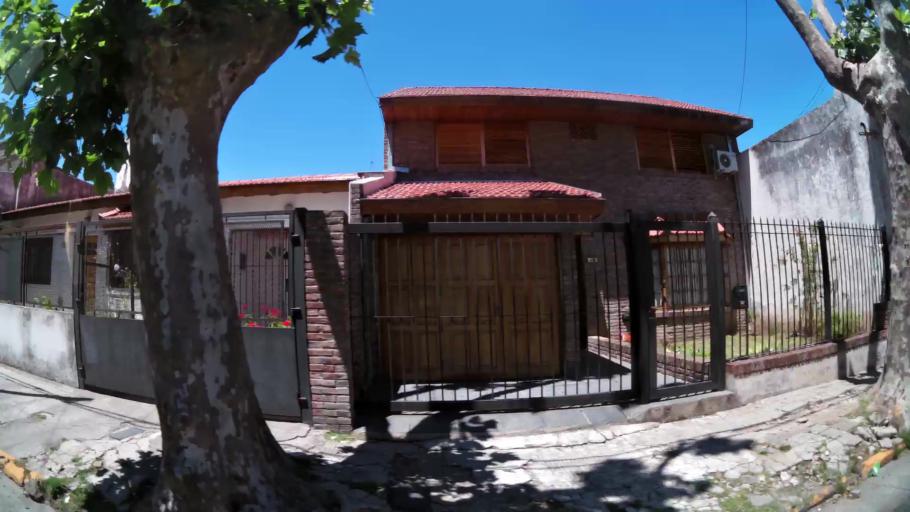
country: AR
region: Buenos Aires
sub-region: Partido de Tigre
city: Tigre
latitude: -34.4451
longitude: -58.5551
